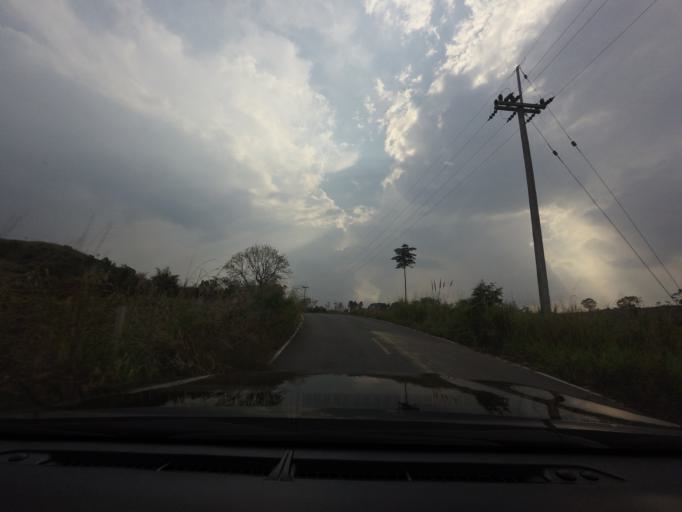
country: TH
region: Nakhon Ratchasima
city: Wang Nam Khiao
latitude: 14.4119
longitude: 101.7934
